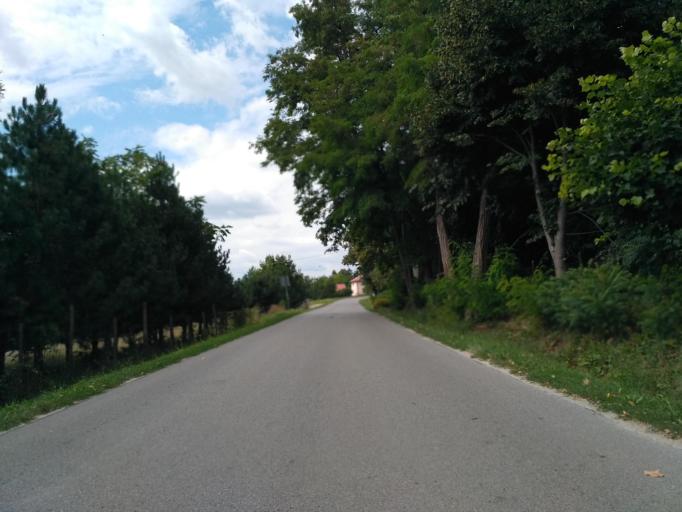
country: PL
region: Subcarpathian Voivodeship
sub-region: Powiat rzeszowski
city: Chmielnik
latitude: 49.9499
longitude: 22.1509
